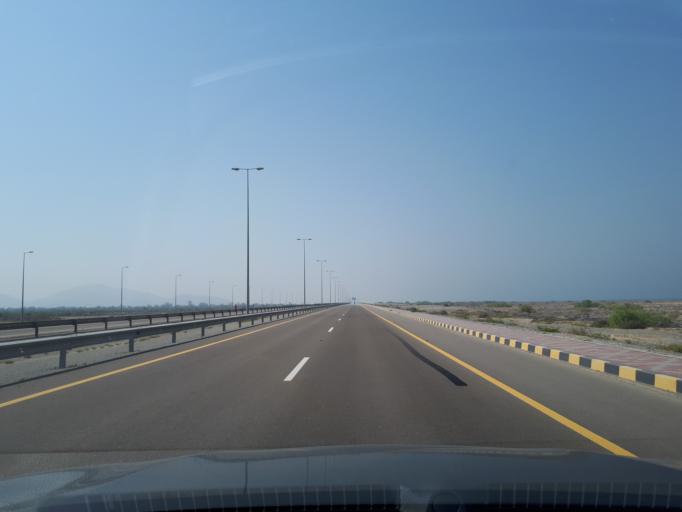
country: AE
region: Al Fujayrah
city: Al Fujayrah
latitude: 24.9325
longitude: 56.3839
